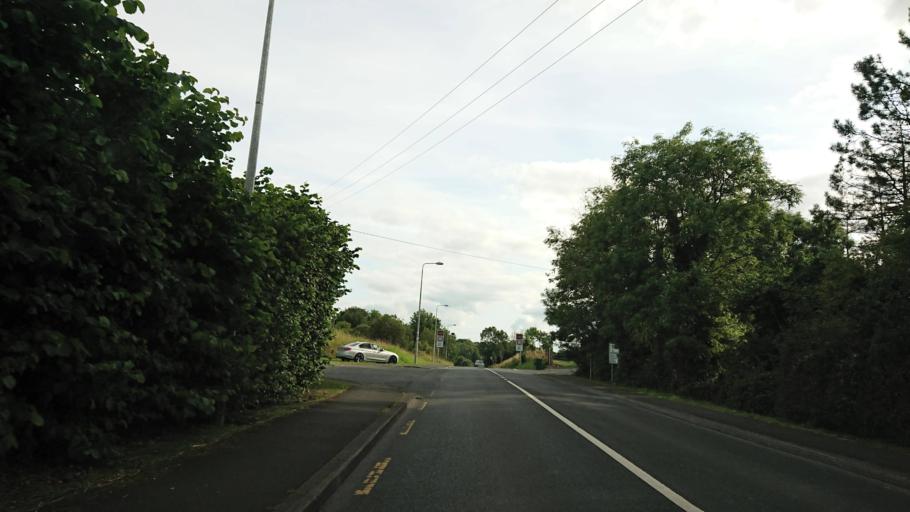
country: IE
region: Connaught
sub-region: County Leitrim
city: Carrick-on-Shannon
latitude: 53.9851
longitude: -8.0645
